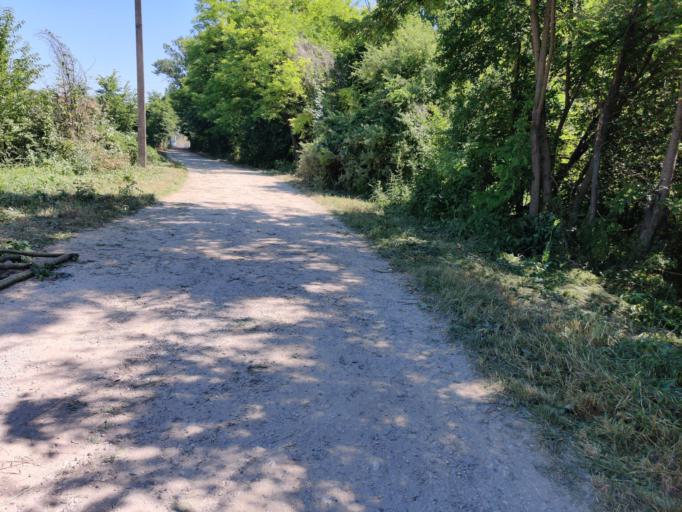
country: HU
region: Hajdu-Bihar
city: Balmazujvaros
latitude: 47.6027
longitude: 21.3788
